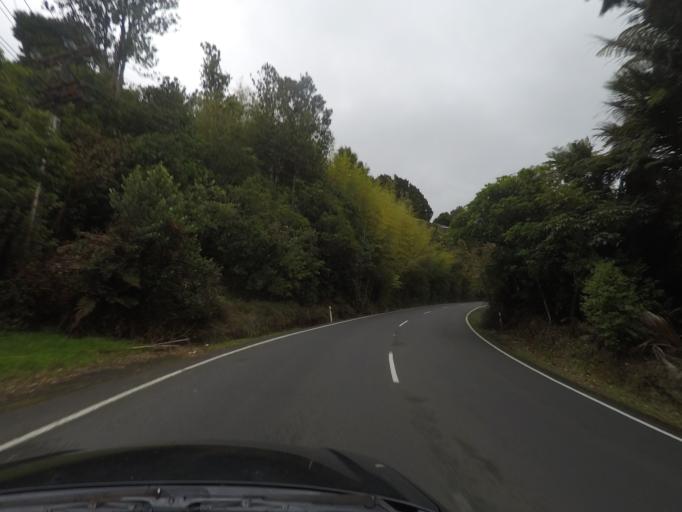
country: NZ
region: Auckland
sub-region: Auckland
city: Titirangi
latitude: -36.9338
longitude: 174.5775
